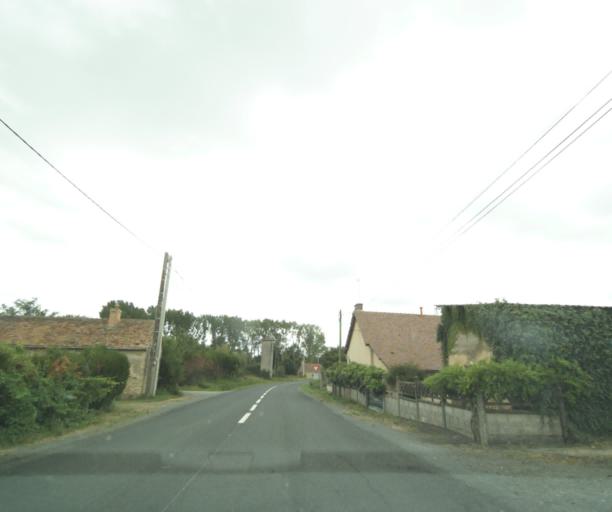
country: FR
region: Pays de la Loire
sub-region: Departement de Maine-et-Loire
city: Durtal
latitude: 47.7185
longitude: -0.2631
